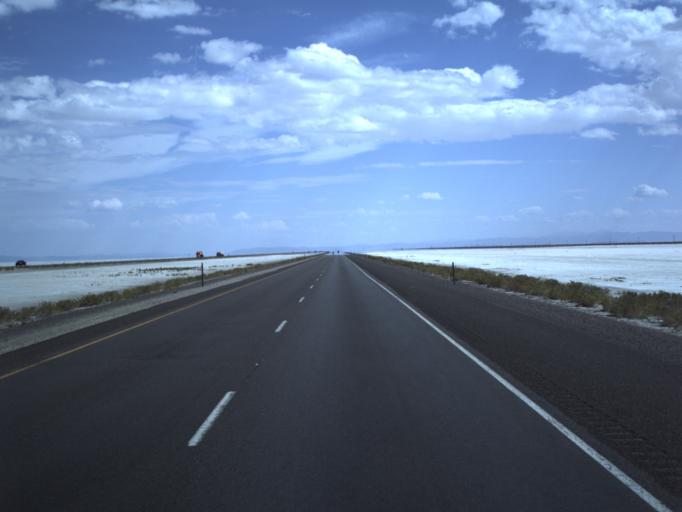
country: US
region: Utah
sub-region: Tooele County
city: Wendover
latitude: 40.7360
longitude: -113.7303
